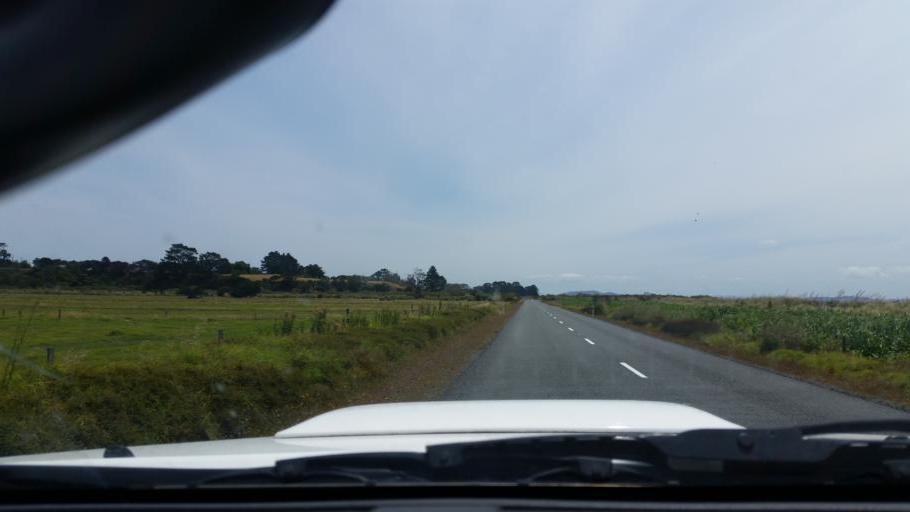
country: NZ
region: Northland
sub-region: Kaipara District
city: Dargaville
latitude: -36.1799
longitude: 174.0301
